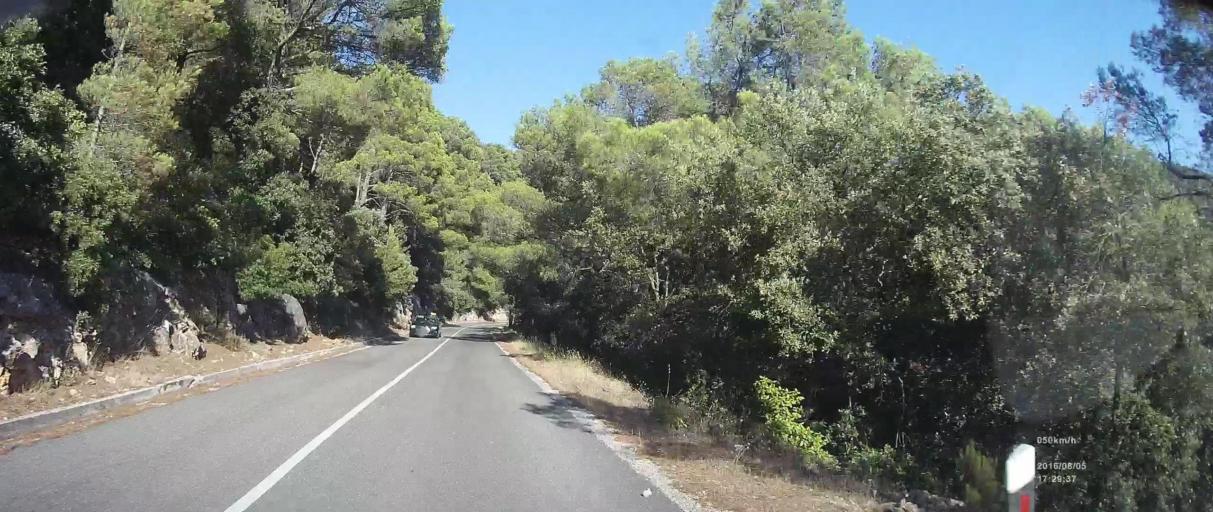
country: HR
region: Dubrovacko-Neretvanska
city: Blato
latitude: 42.7774
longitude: 17.4095
